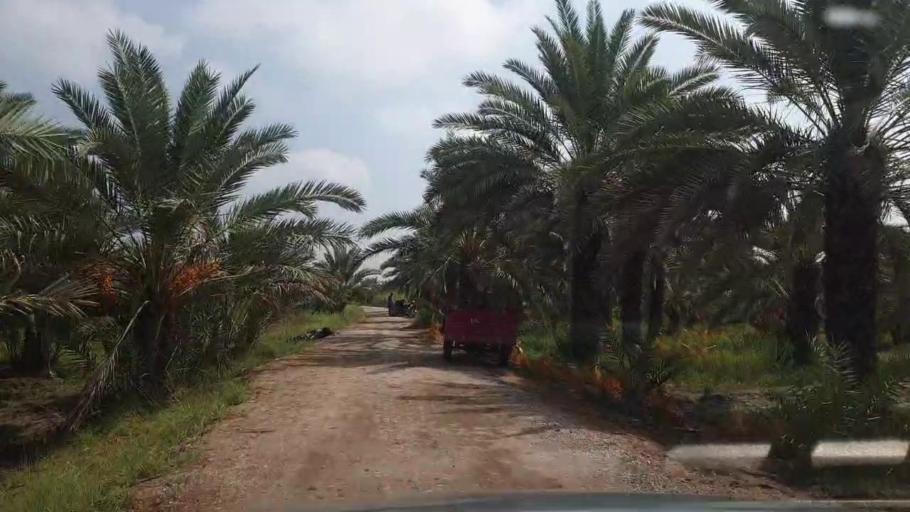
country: PK
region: Sindh
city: Pir jo Goth
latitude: 27.6030
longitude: 68.6956
